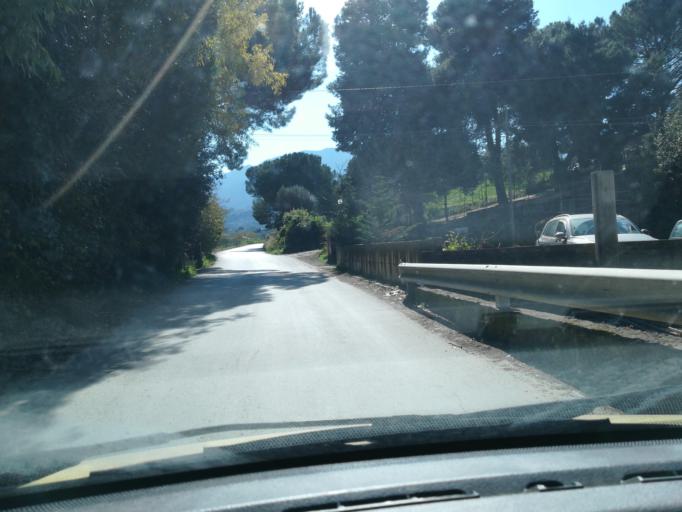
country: IT
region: Sicily
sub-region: Palermo
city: Cannizzaro-Favara
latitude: 38.0508
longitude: 13.2594
